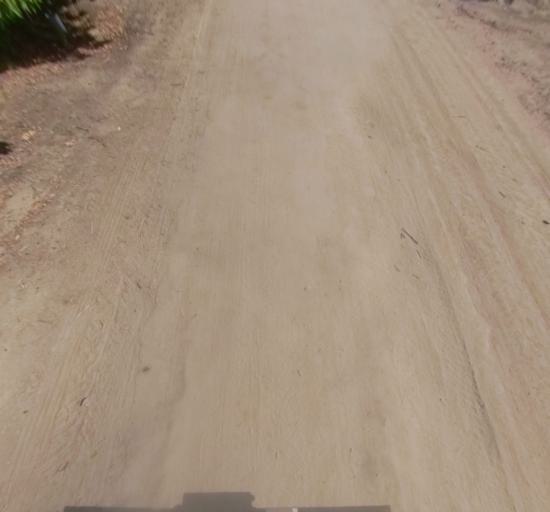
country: US
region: California
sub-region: Madera County
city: Parkwood
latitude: 36.8854
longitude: -120.1467
